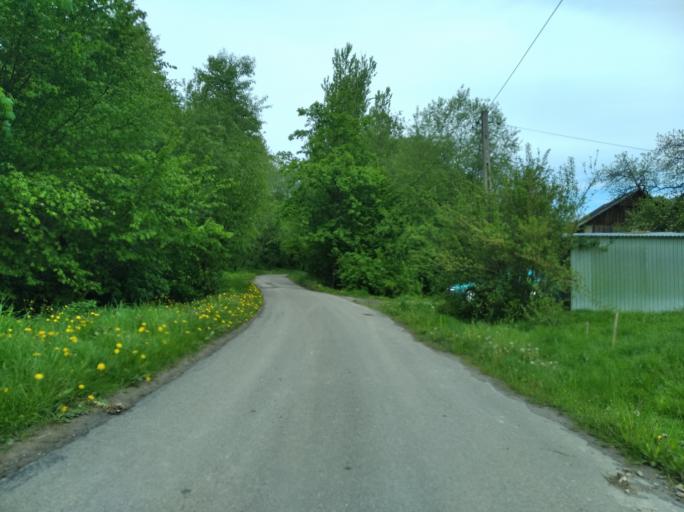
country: PL
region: Subcarpathian Voivodeship
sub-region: Powiat strzyzowski
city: Strzyzow
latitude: 49.9156
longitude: 21.7599
